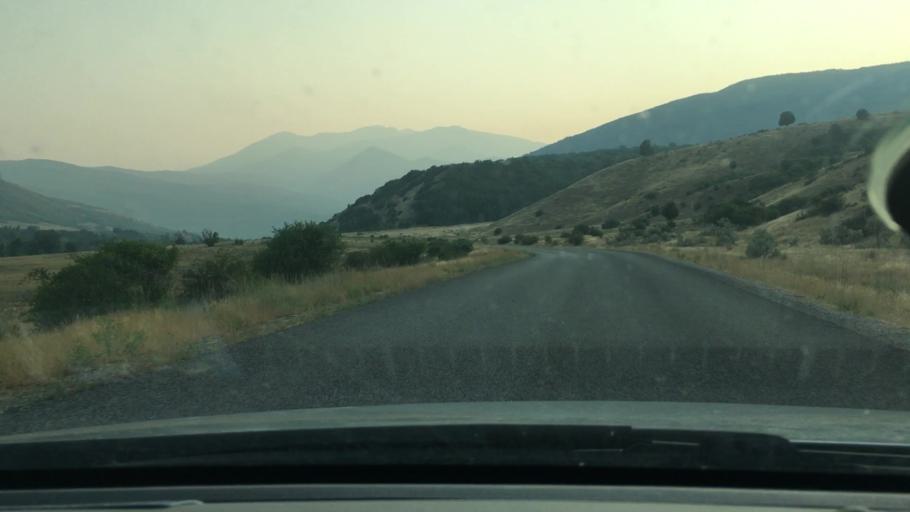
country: US
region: Utah
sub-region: Utah County
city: Mapleton
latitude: 40.0463
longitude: -111.4733
